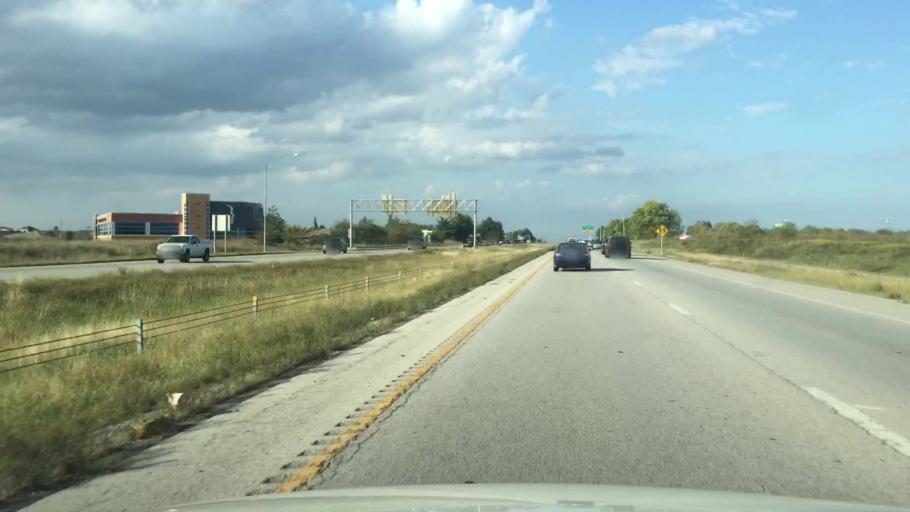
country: US
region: Missouri
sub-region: Jackson County
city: Lees Summit
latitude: 38.9695
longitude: -94.3582
